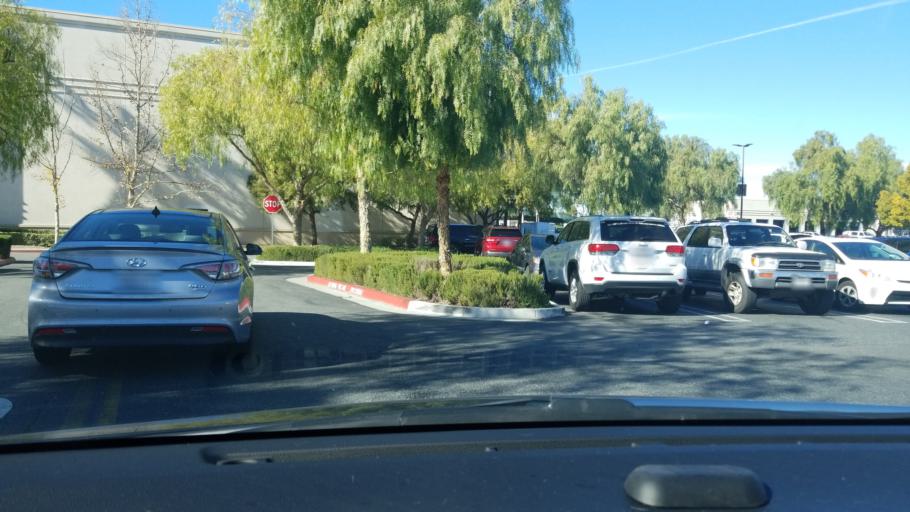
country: US
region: California
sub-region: Riverside County
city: Temecula
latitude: 33.5261
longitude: -117.1523
